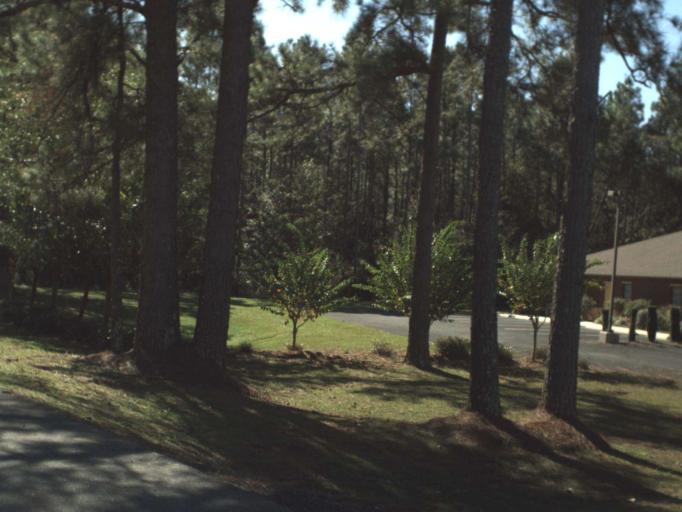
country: US
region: Florida
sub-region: Okaloosa County
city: Crestview
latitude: 30.7871
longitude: -86.6838
